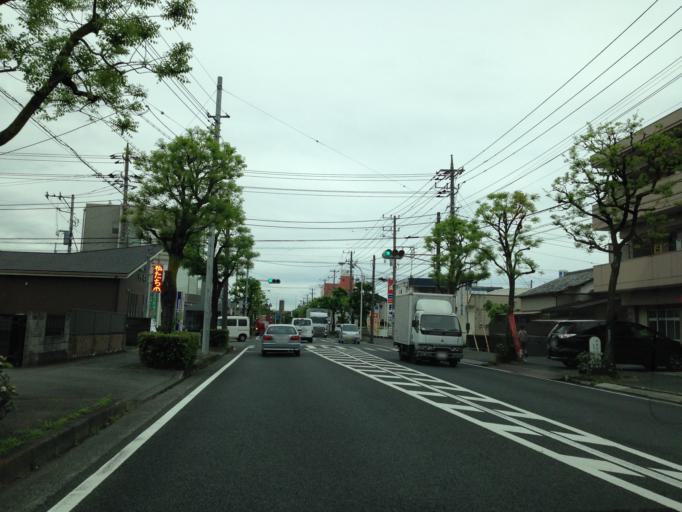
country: JP
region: Shizuoka
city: Fuji
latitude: 35.1586
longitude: 138.6873
